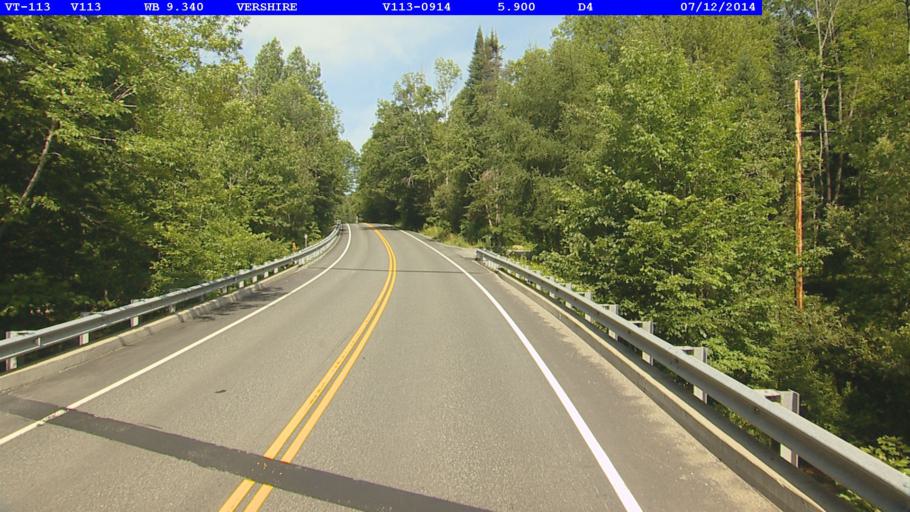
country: US
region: New Hampshire
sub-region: Grafton County
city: Orford
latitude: 43.9594
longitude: -72.2815
